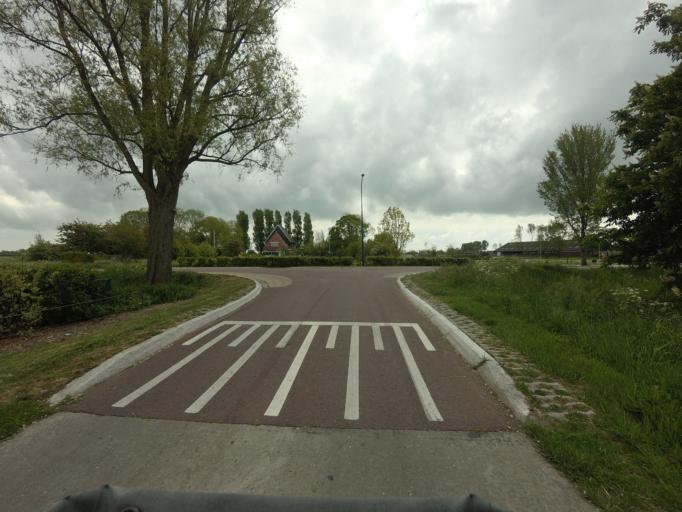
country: NL
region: Friesland
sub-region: Gemeente Littenseradiel
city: Wommels
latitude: 53.1027
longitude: 5.6240
